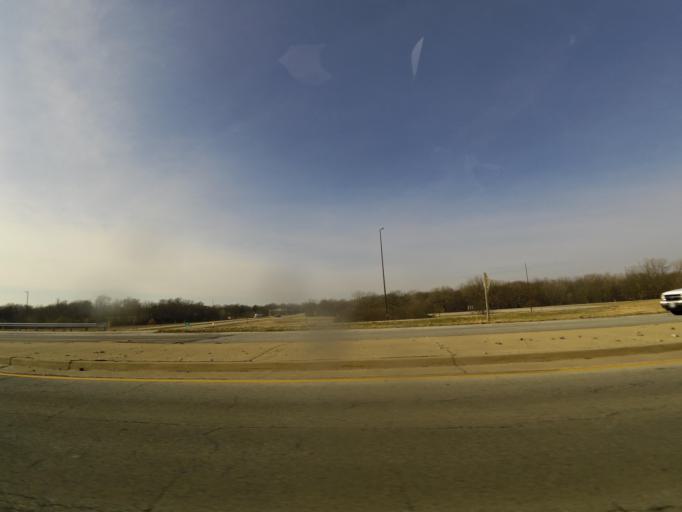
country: US
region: Illinois
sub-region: Macon County
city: Forsyth
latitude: 39.9091
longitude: -88.9552
